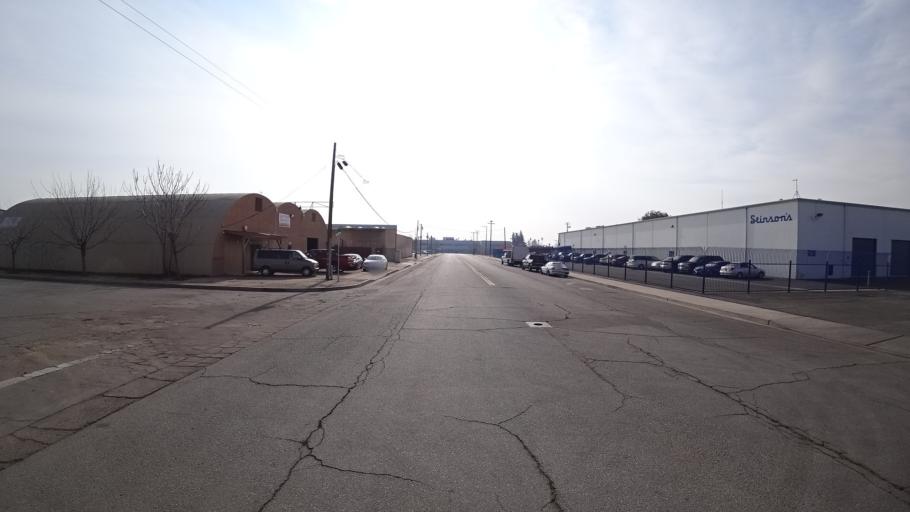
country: US
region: California
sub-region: Kern County
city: Bakersfield
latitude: 35.3721
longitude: -119.0013
